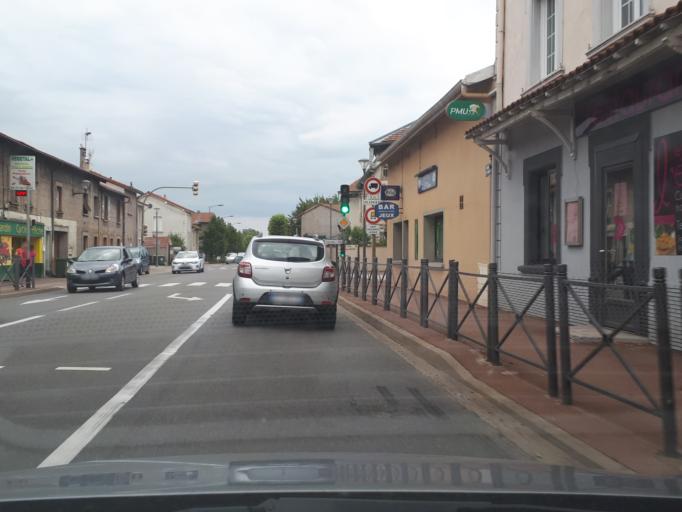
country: FR
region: Rhone-Alpes
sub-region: Departement de la Loire
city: Veauche
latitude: 45.5623
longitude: 4.2769
